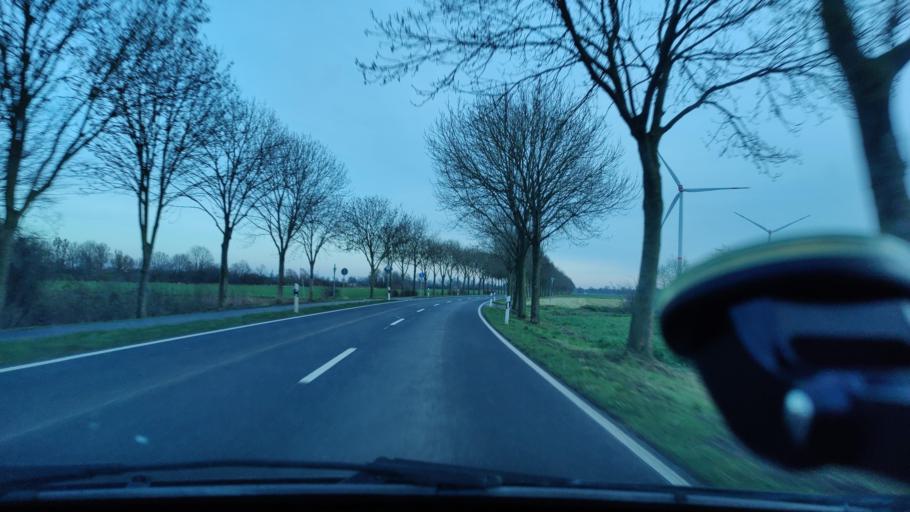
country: DE
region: North Rhine-Westphalia
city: Kalkar
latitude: 51.7508
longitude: 6.3159
